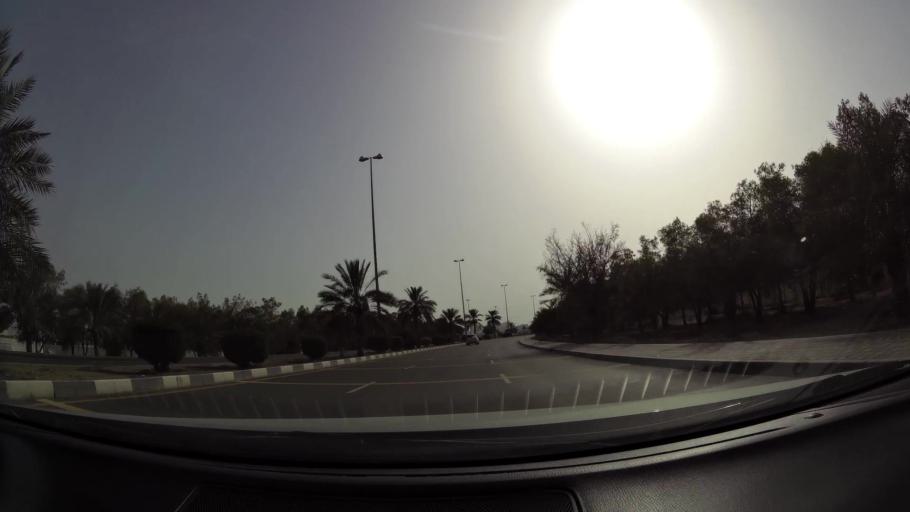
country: AE
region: Abu Dhabi
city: Al Ain
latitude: 24.1345
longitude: 55.7104
